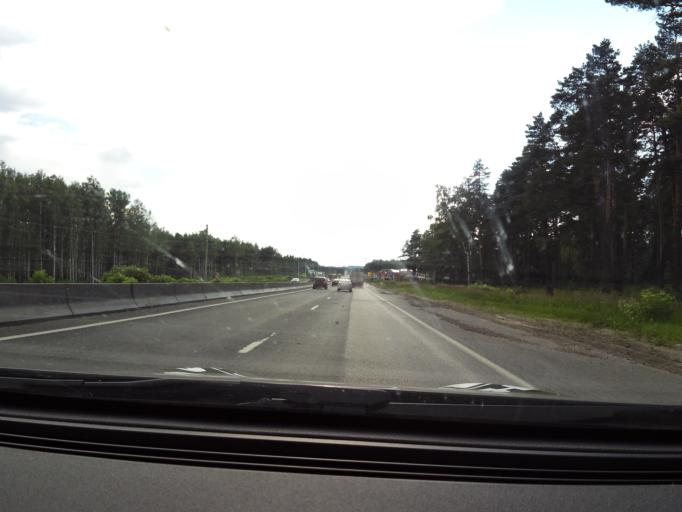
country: RU
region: Nizjnij Novgorod
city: Novosmolinskiy
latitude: 56.2790
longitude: 43.0315
